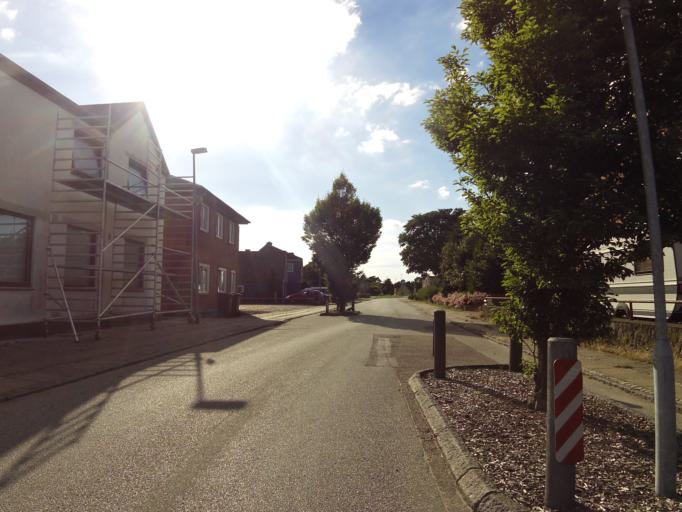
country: DK
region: South Denmark
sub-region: Haderslev Kommune
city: Vojens
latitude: 55.1972
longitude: 9.2987
